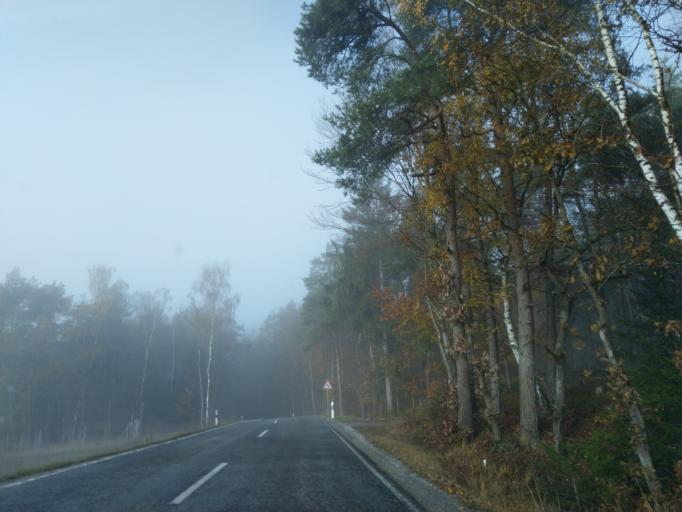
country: DE
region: Bavaria
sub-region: Lower Bavaria
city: Aussernzell
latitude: 48.7299
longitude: 13.1801
